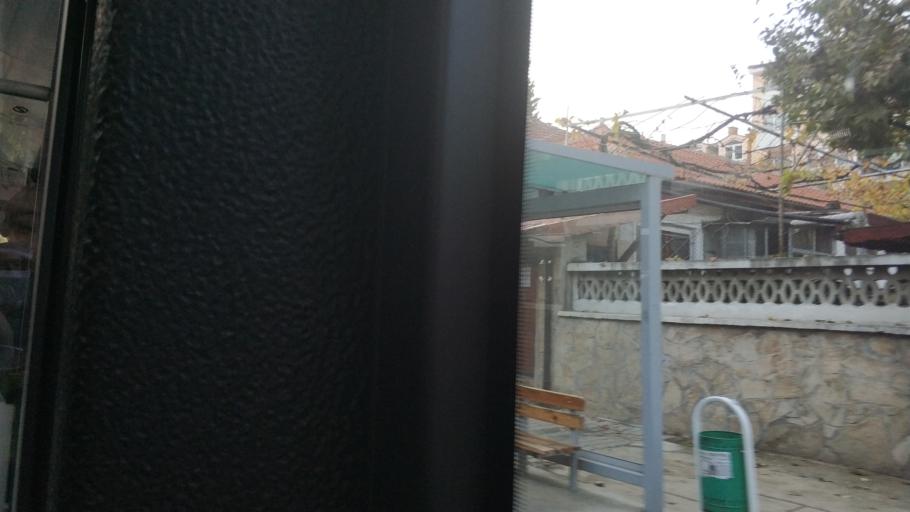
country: BG
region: Stara Zagora
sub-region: Obshtina Stara Zagora
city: Stara Zagora
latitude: 42.4197
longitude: 25.6177
